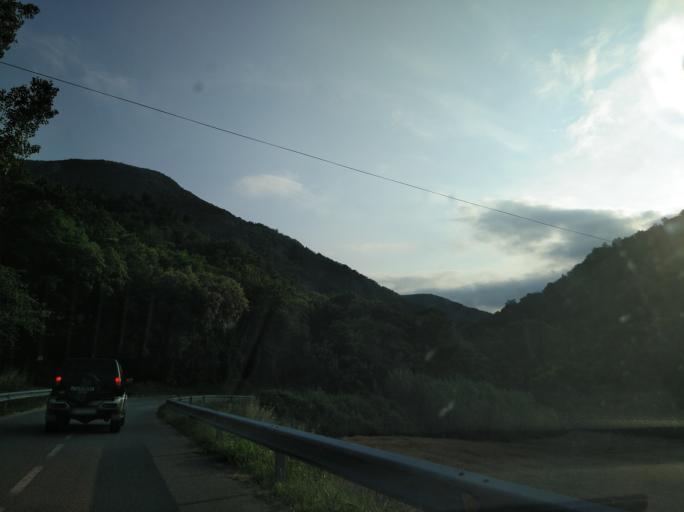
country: ES
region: Catalonia
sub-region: Provincia de Girona
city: Angles
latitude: 41.9514
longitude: 2.6184
